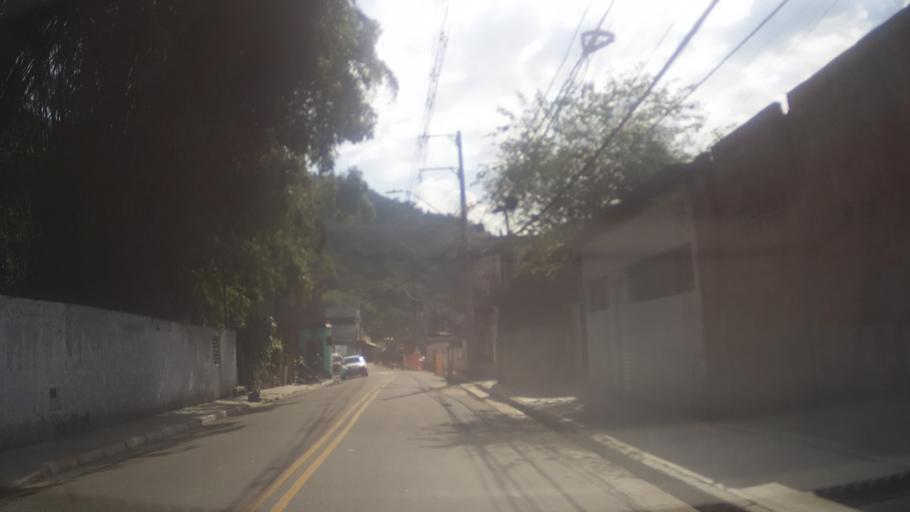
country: BR
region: Sao Paulo
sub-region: Santos
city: Santos
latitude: -23.9348
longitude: -46.3516
